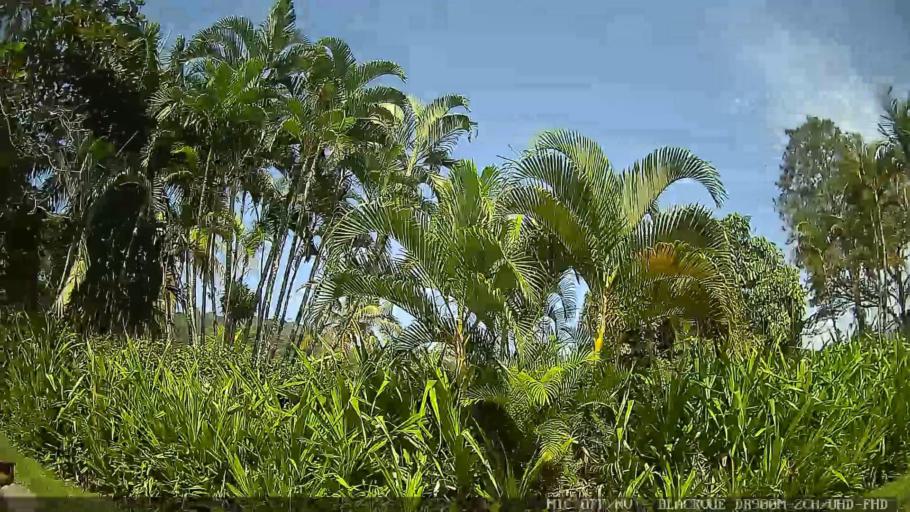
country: BR
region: Sao Paulo
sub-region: Guaruja
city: Guaruja
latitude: -23.9793
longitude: -46.1980
